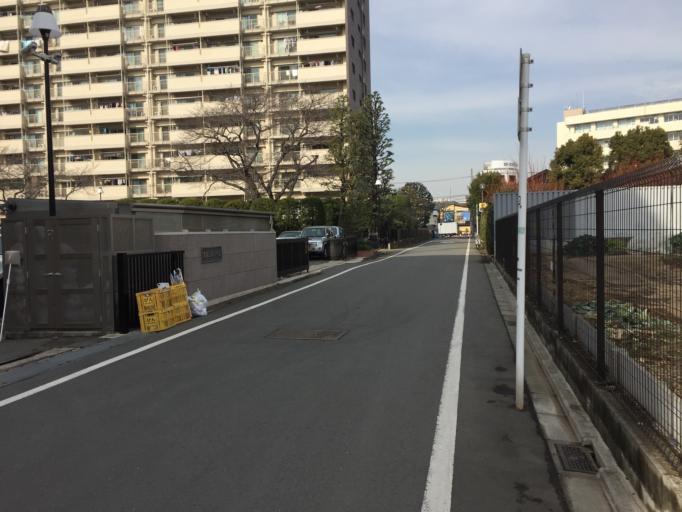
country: JP
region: Tokyo
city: Tokyo
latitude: 35.6388
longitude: 139.6312
